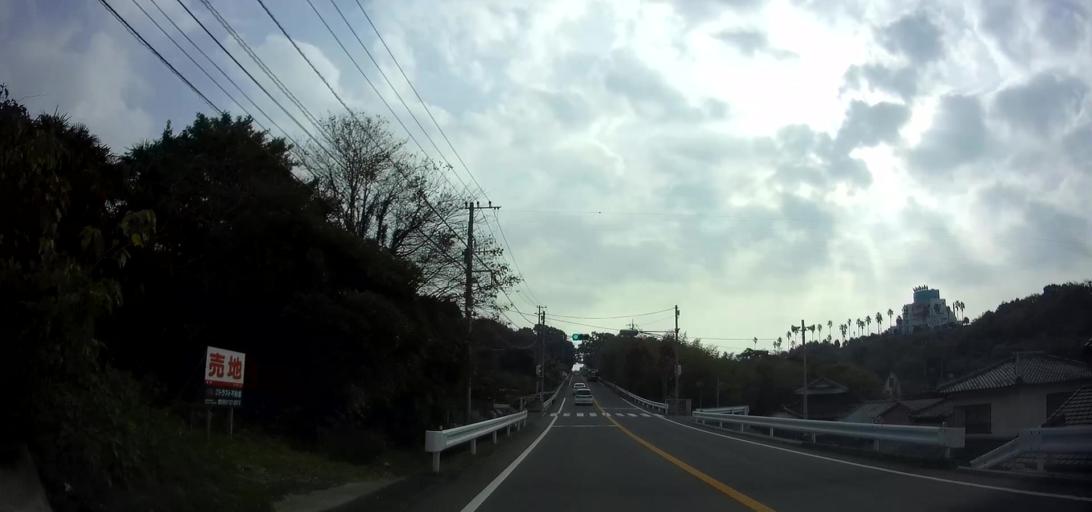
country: JP
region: Nagasaki
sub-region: Isahaya-shi
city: Isahaya
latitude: 32.7971
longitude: 130.0923
